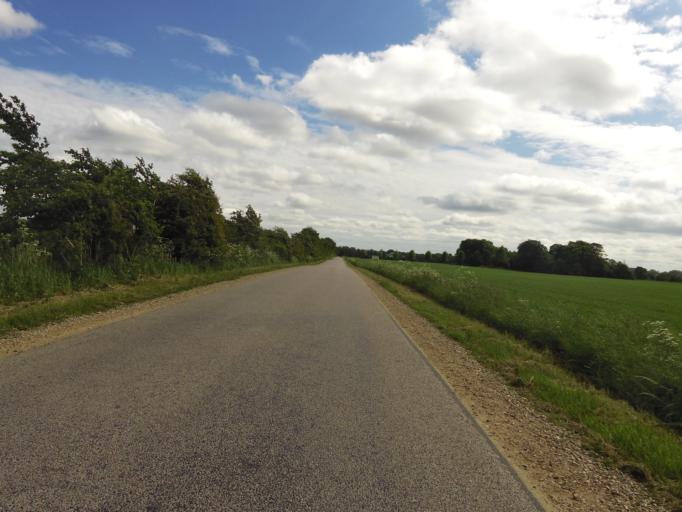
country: DK
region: South Denmark
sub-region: Vejen Kommune
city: Vejen
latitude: 55.4433
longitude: 9.1086
